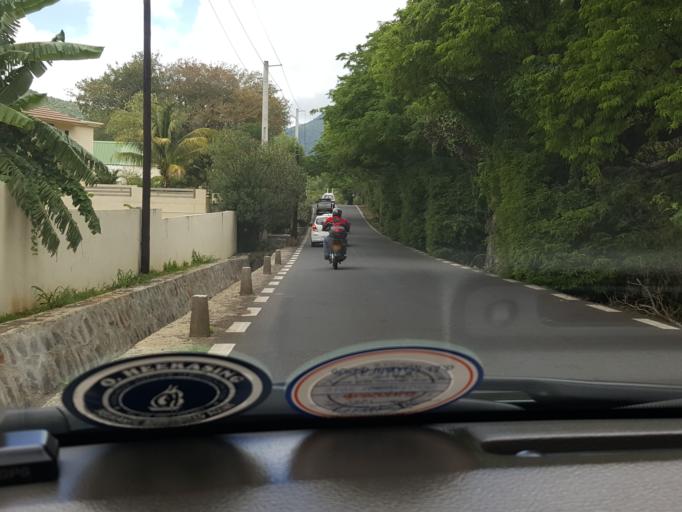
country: MU
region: Black River
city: Petite Case Noyale
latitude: -20.3880
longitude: 57.3820
